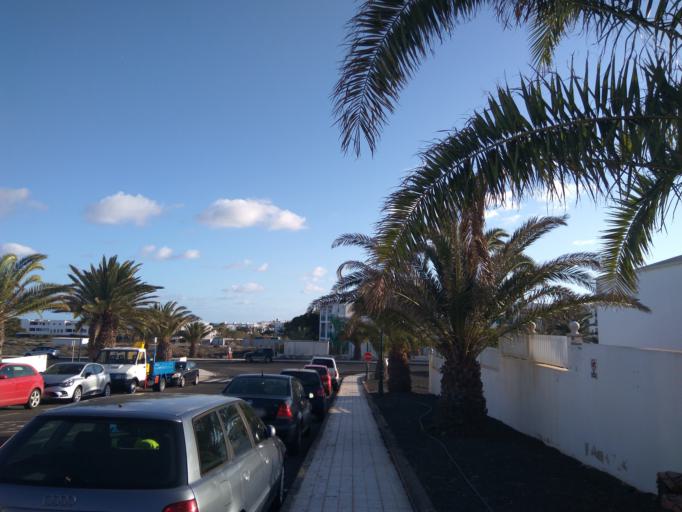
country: ES
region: Canary Islands
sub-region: Provincia de Las Palmas
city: Arrecife
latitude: 29.0056
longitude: -13.4906
